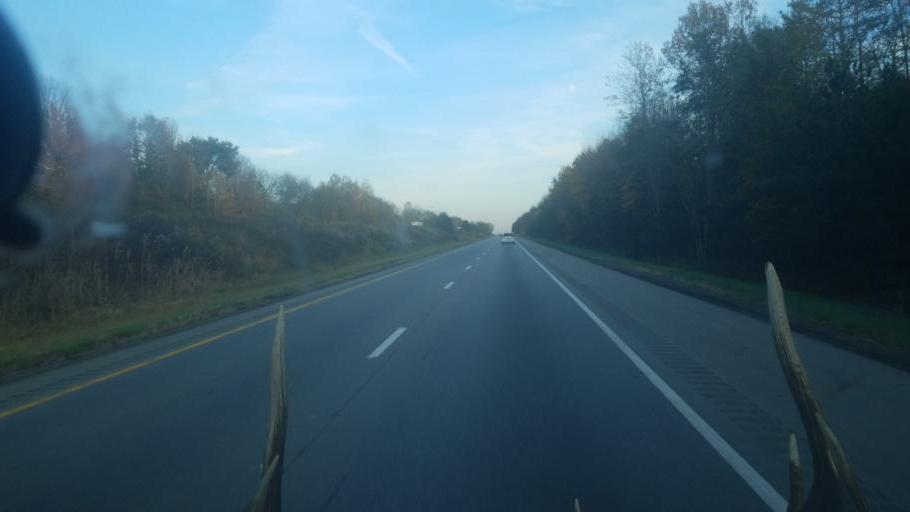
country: US
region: Ohio
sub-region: Muskingum County
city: Zanesville
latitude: 39.9511
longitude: -82.1763
